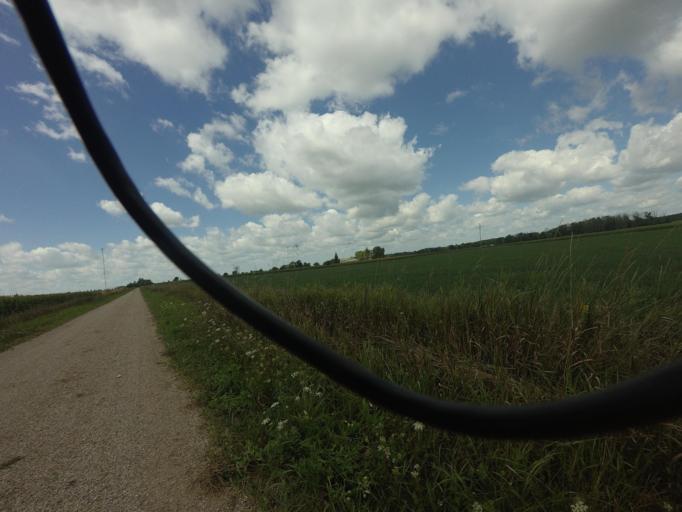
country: CA
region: Ontario
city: North Perth
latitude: 43.5671
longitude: -80.9389
